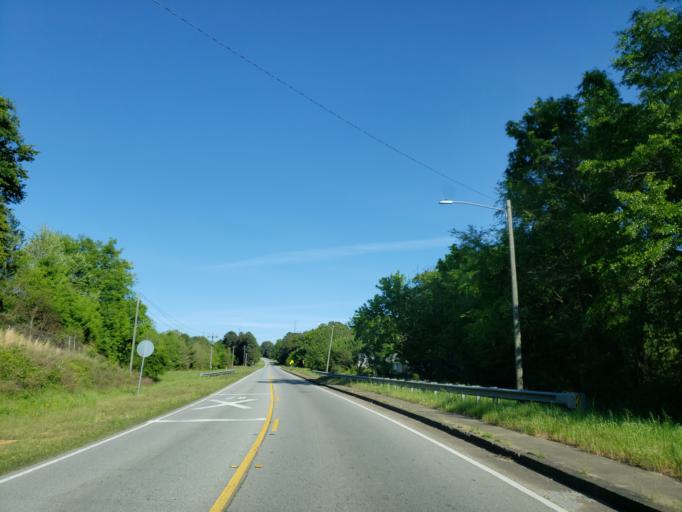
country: US
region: Georgia
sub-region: Polk County
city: Cedartown
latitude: 34.0029
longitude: -85.2485
